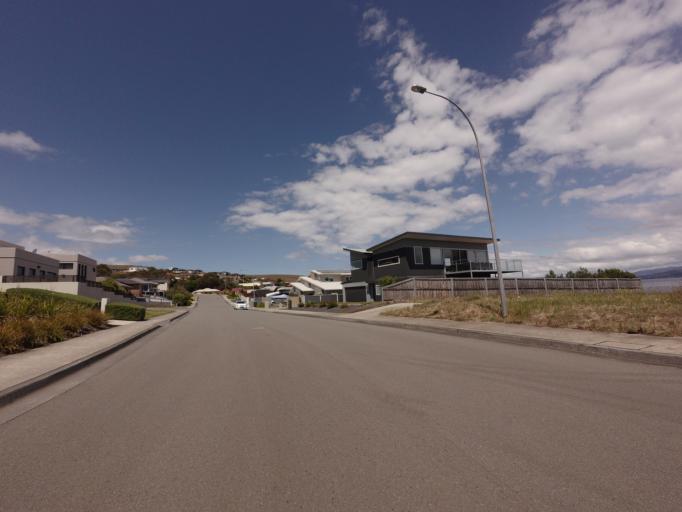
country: AU
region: Tasmania
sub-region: Clarence
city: Howrah
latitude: -42.9194
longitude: 147.4108
